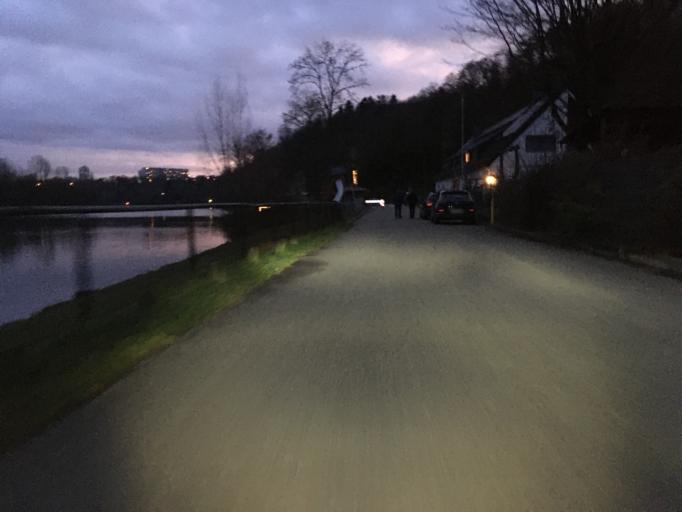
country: DE
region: Baden-Wuerttemberg
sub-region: Regierungsbezirk Stuttgart
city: Stuttgart Muehlhausen
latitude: 48.8329
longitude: 9.2075
